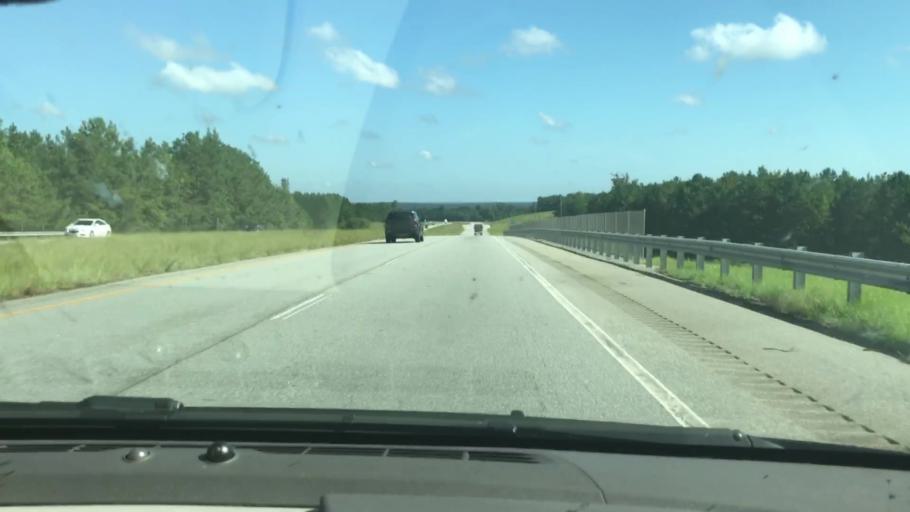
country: US
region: Alabama
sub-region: Barbour County
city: Eufaula
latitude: 32.1605
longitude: -85.1778
